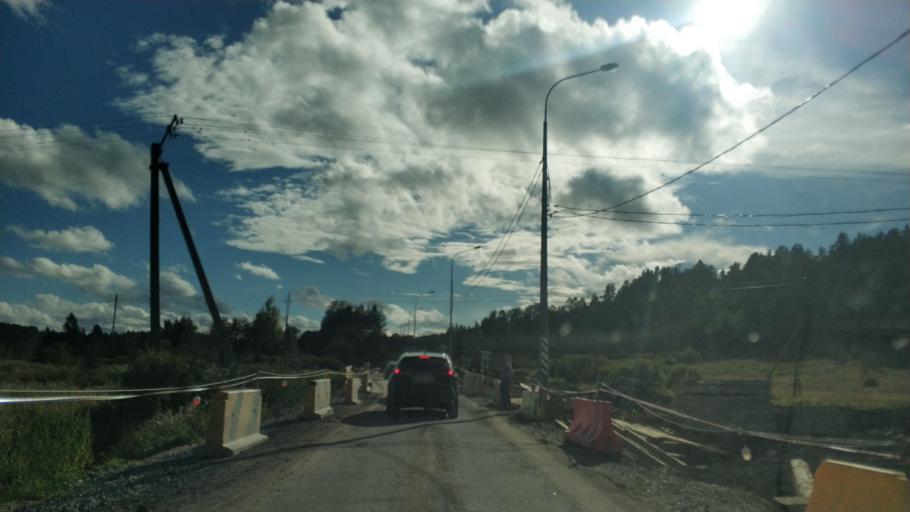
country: RU
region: Republic of Karelia
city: Lakhdenpokh'ya
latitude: 61.5573
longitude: 30.3262
